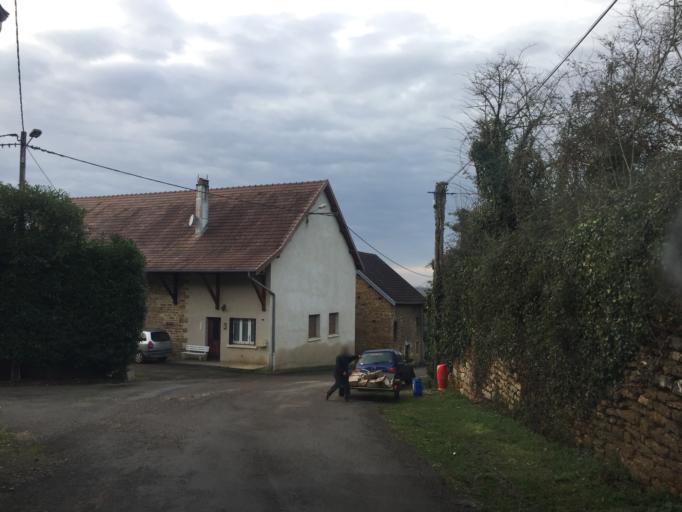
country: FR
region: Franche-Comte
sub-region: Departement du Jura
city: Mont-sous-Vaudrey
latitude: 46.9394
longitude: 5.6859
